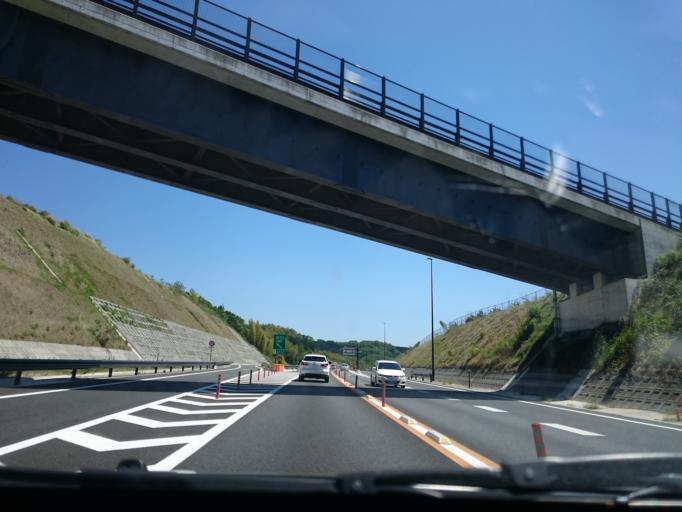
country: JP
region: Shizuoka
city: Mishima
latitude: 35.1239
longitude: 138.9479
